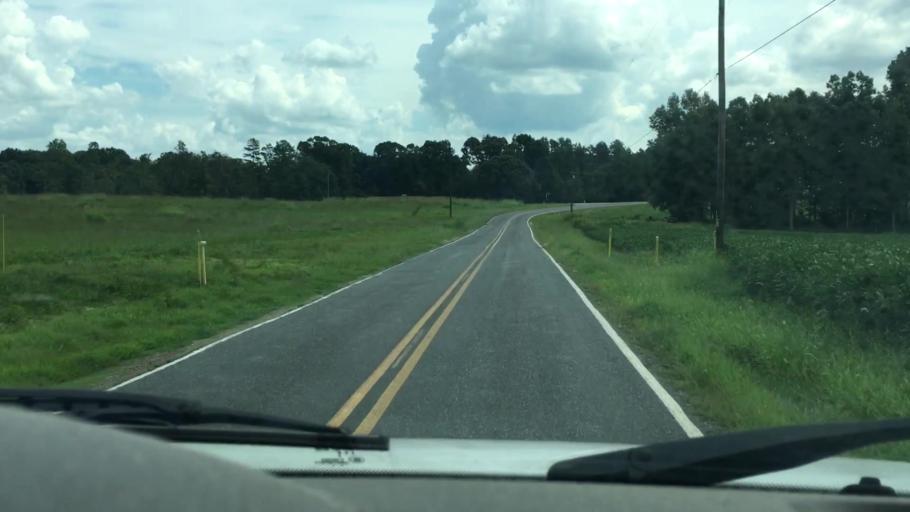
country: US
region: North Carolina
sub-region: Iredell County
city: Troutman
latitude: 35.6760
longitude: -80.8442
